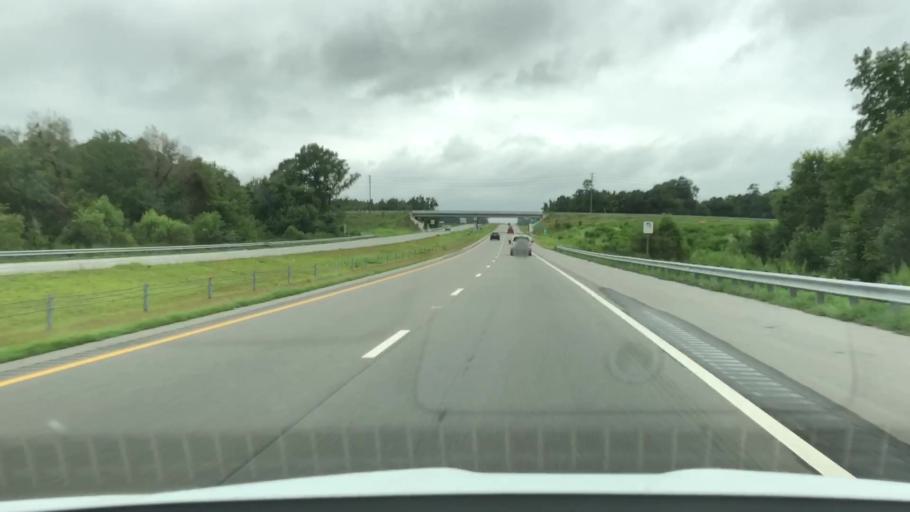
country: US
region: North Carolina
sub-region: Lenoir County
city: La Grange
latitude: 35.3093
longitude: -77.8226
